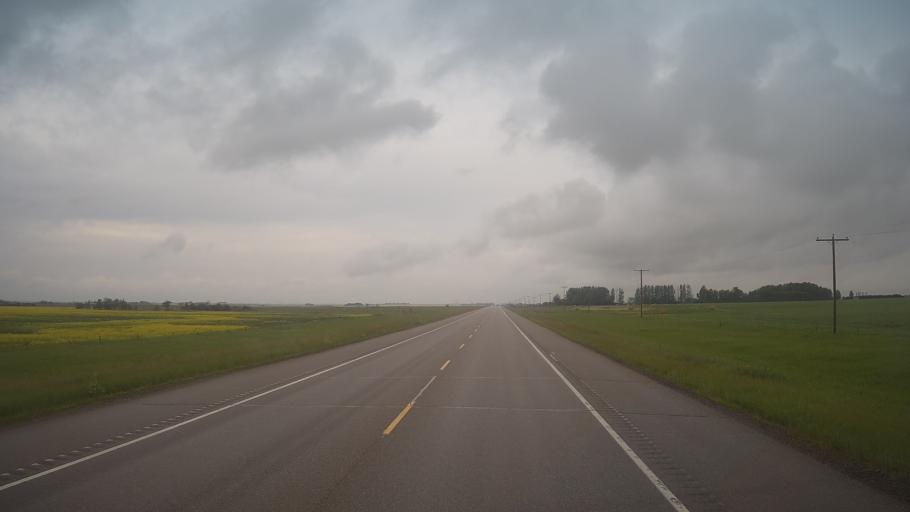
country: CA
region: Saskatchewan
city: Unity
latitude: 52.4349
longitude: -108.9666
